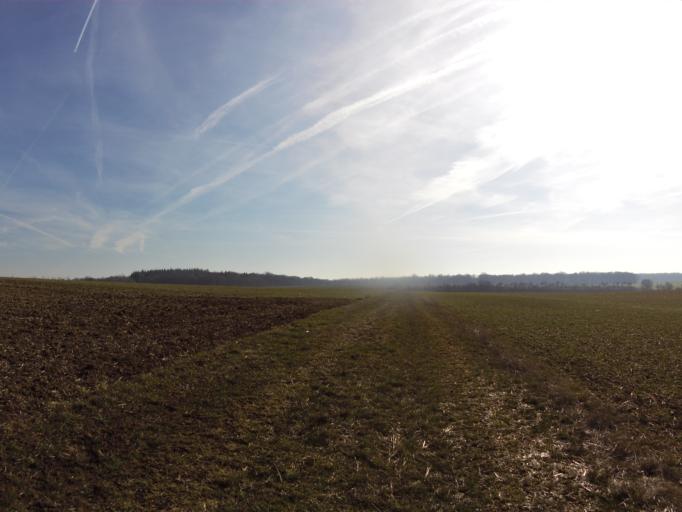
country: DE
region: Bavaria
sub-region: Regierungsbezirk Unterfranken
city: Rottendorf
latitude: 49.8246
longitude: 10.0352
